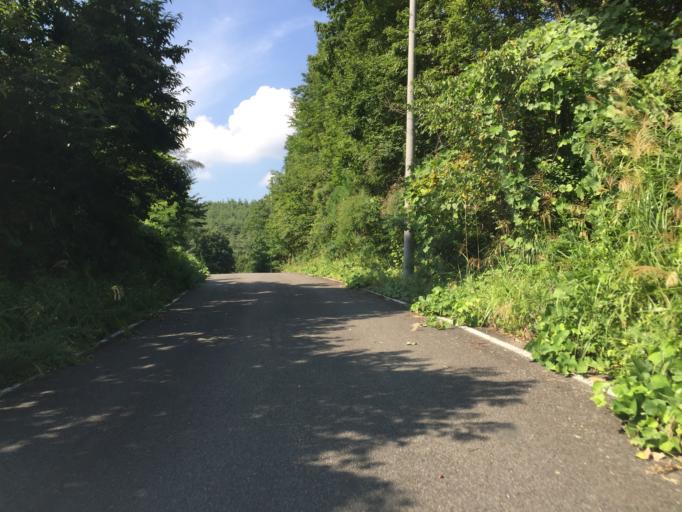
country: JP
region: Fukushima
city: Nihommatsu
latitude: 37.6076
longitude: 140.3852
